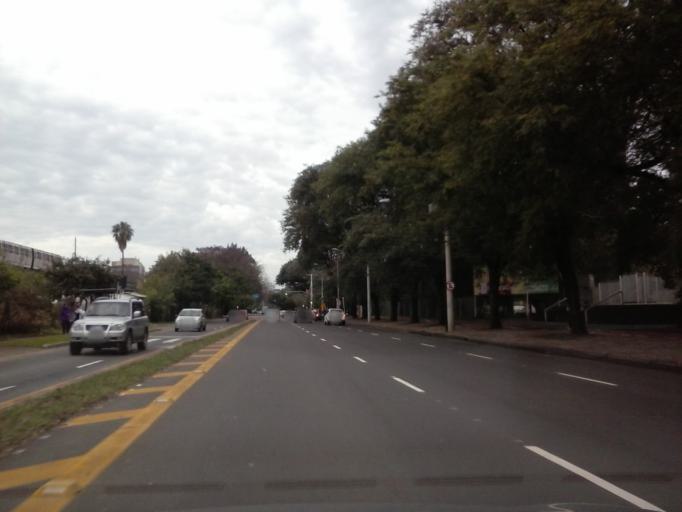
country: BR
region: Rio Grande do Sul
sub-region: Porto Alegre
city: Porto Alegre
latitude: -30.0371
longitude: -51.2389
